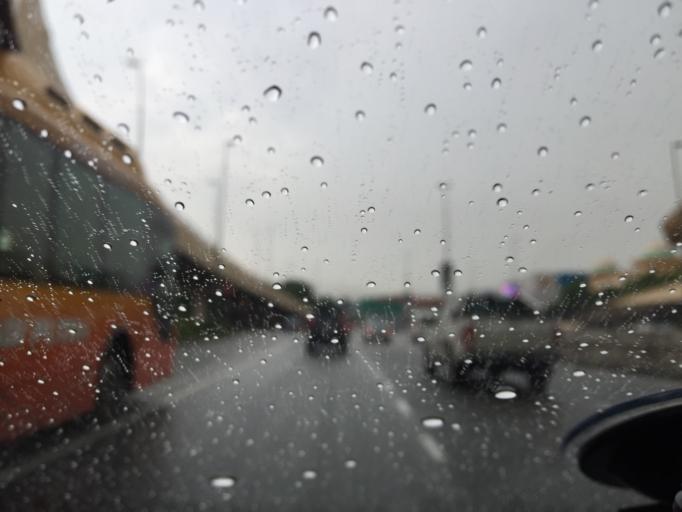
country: MY
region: Selangor
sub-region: Petaling
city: Petaling Jaya
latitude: 3.0741
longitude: 101.6062
